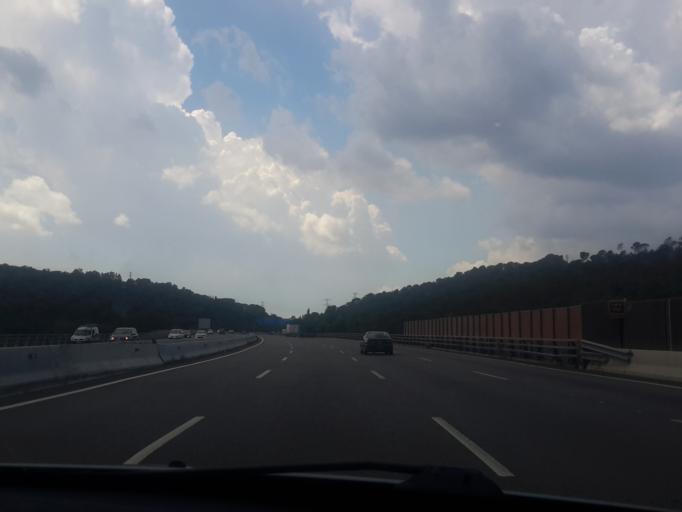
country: ES
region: Catalonia
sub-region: Provincia de Girona
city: Sarria de Ter
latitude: 42.0098
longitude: 2.8092
